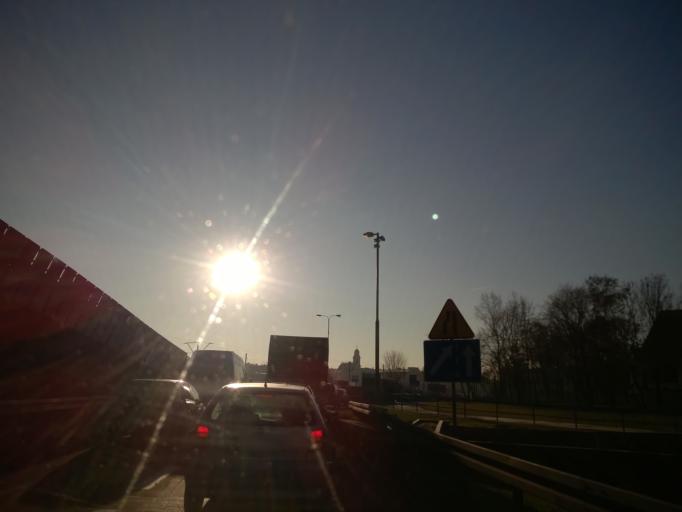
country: PL
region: Lower Silesian Voivodeship
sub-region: Powiat wroclawski
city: Wroclaw
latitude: 51.1075
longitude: 17.0477
